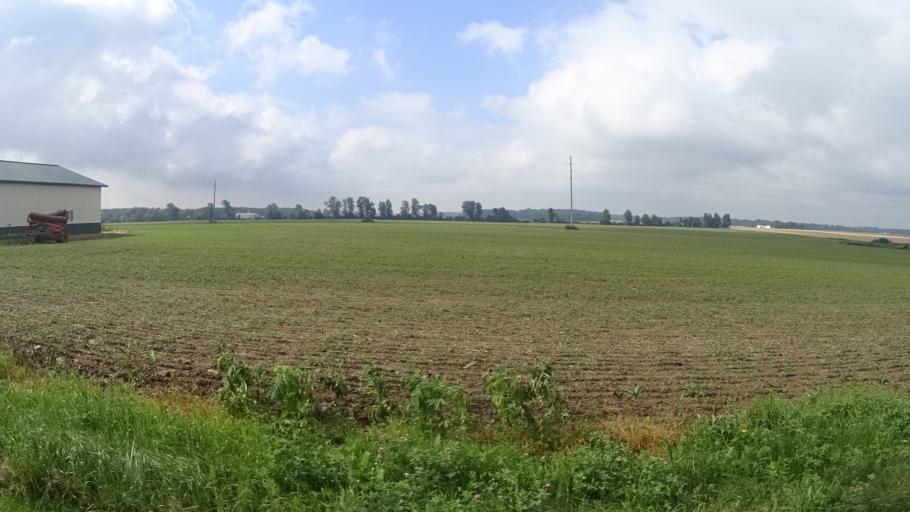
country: US
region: Ohio
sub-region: Huron County
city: Wakeman
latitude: 41.2839
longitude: -82.4473
